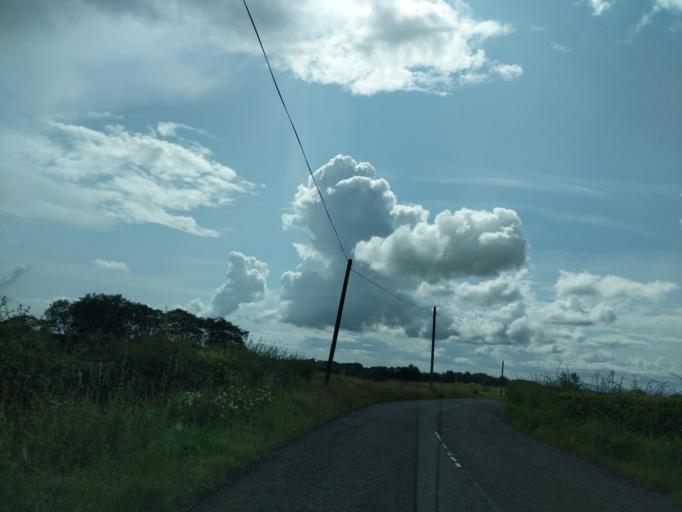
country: GB
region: Scotland
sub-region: East Ayrshire
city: Stewarton
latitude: 55.7258
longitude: -4.4836
